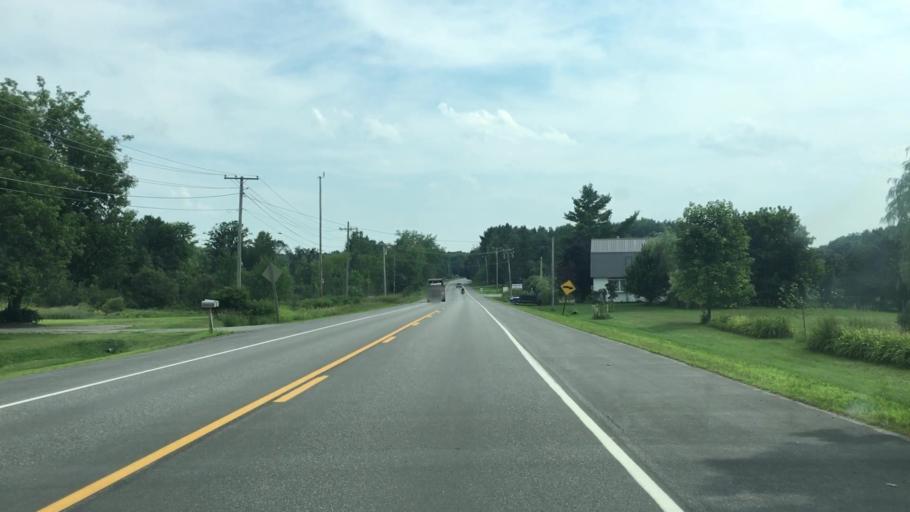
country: US
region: Maine
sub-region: Kennebec County
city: Windsor
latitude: 44.3925
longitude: -69.5708
